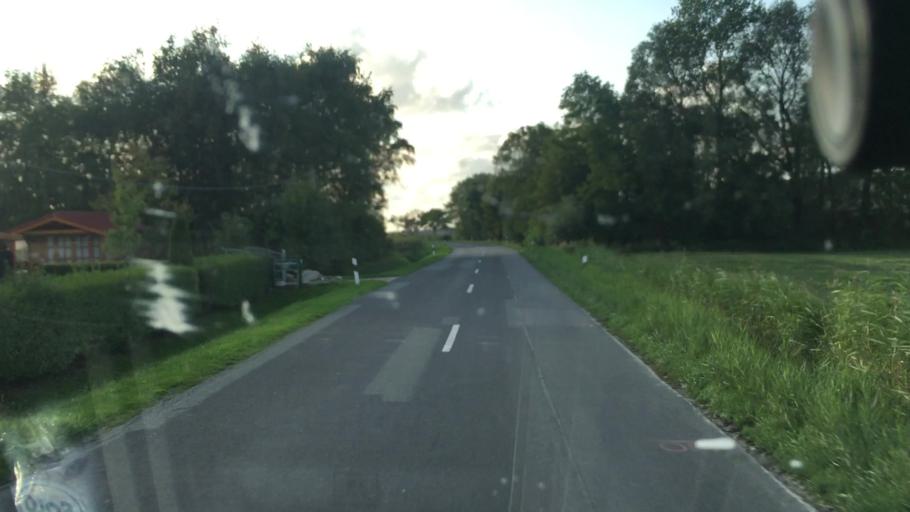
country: DE
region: Lower Saxony
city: Werdum
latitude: 53.6677
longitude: 7.7291
